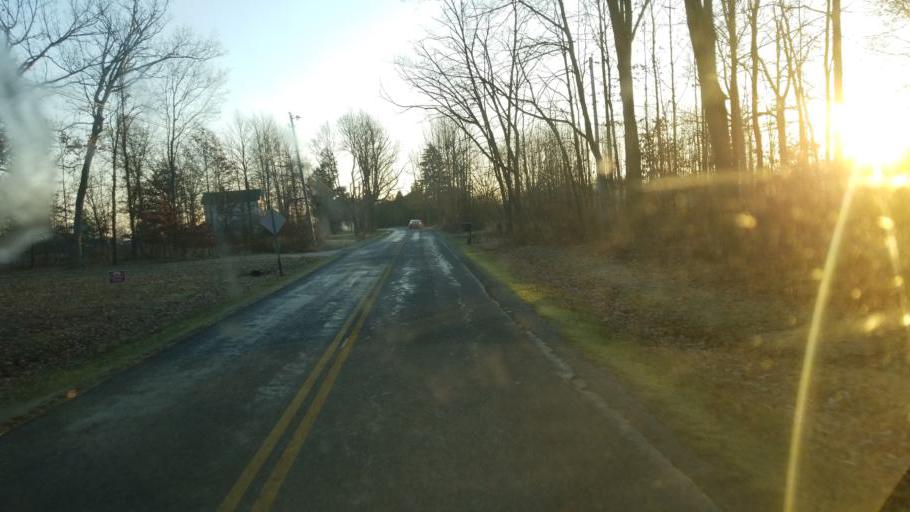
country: US
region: Ohio
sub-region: Medina County
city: Lodi
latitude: 41.0399
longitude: -81.9869
